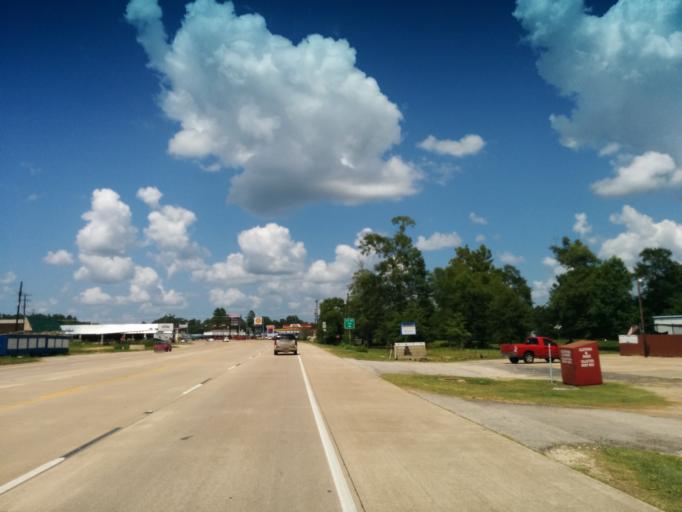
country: US
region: Texas
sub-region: Jasper County
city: Buna
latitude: 30.4395
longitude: -93.9707
